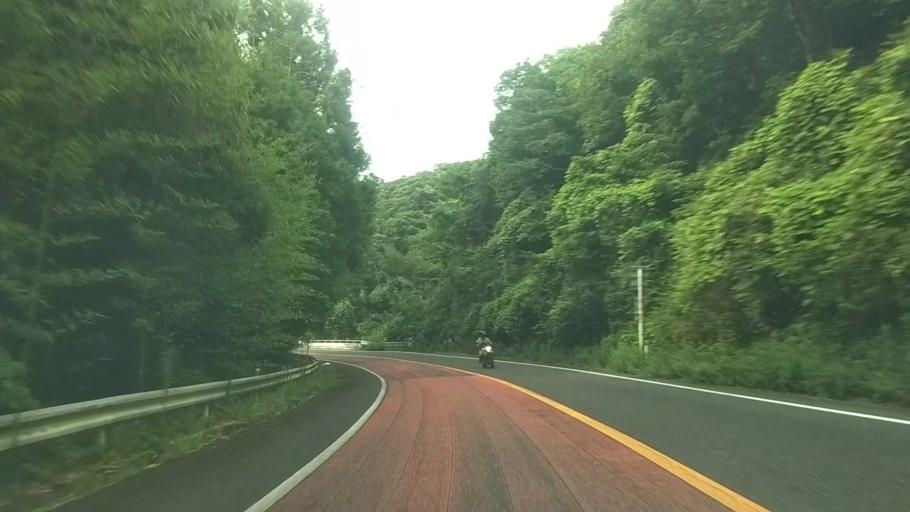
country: JP
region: Chiba
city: Kimitsu
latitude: 35.2459
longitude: 140.0057
